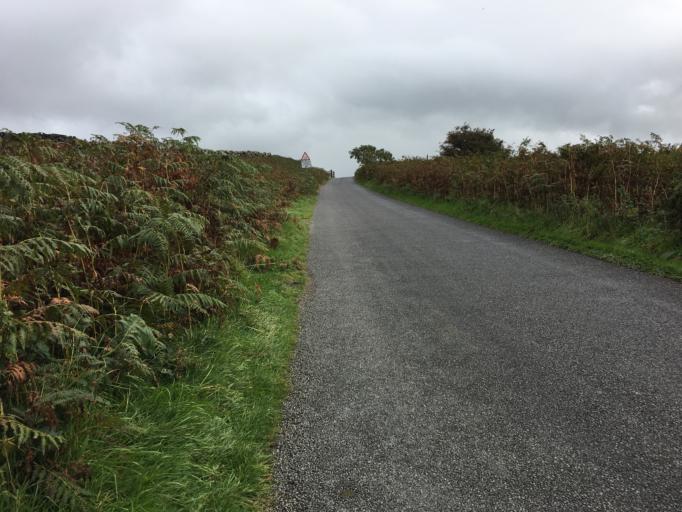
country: GB
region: England
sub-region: North Yorkshire
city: Danby
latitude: 54.4673
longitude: -0.8850
